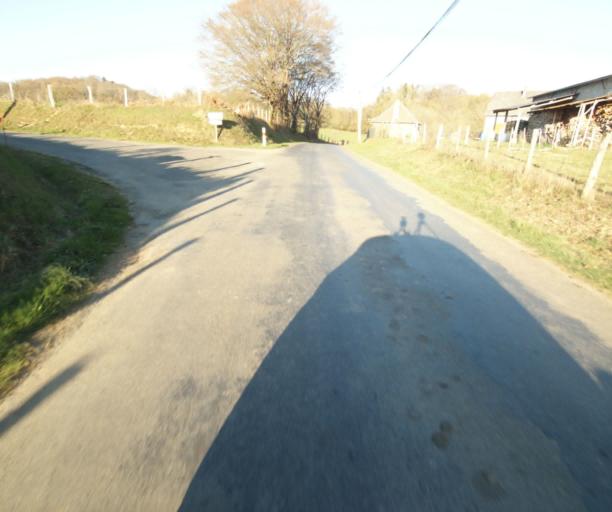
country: FR
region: Limousin
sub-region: Departement de la Correze
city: Saint-Clement
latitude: 45.3508
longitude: 1.6547
